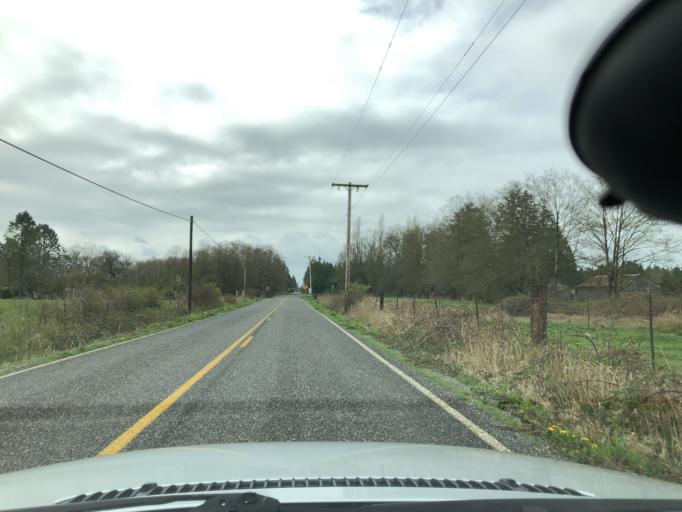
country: CA
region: British Columbia
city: Langley
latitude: 48.9732
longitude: -122.6159
